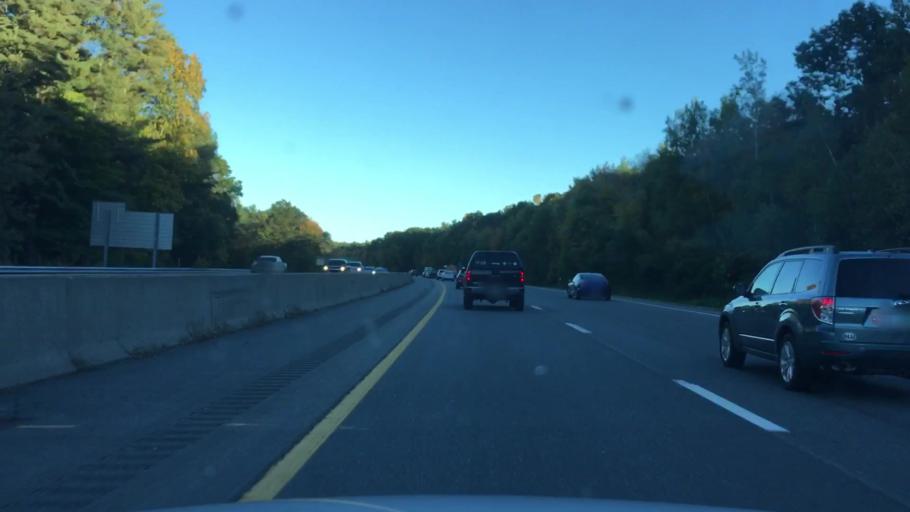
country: US
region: New Hampshire
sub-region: Rockingham County
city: Hampton Falls
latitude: 42.9678
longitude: -70.8874
